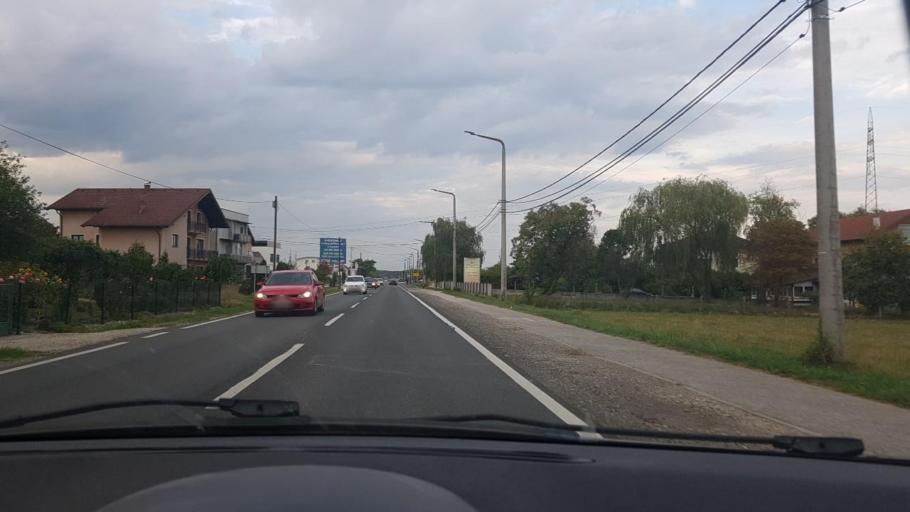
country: HR
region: Grad Zagreb
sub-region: Sesvete
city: Sesvete
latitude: 45.8679
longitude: 16.1577
